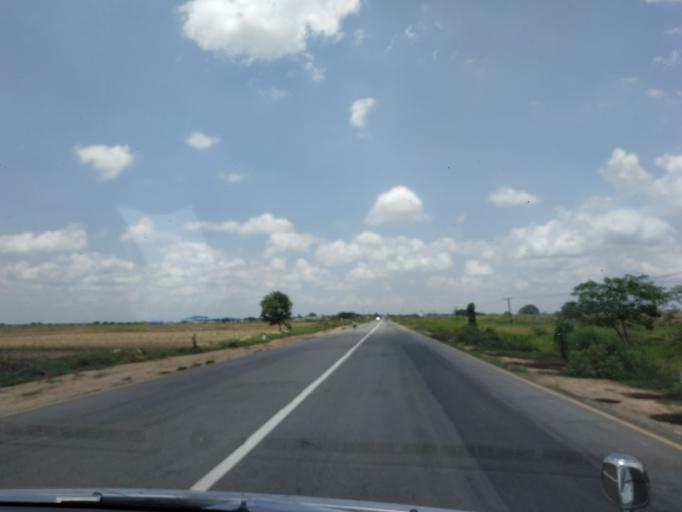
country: MM
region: Bago
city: Thanatpin
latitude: 17.4593
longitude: 96.6002
